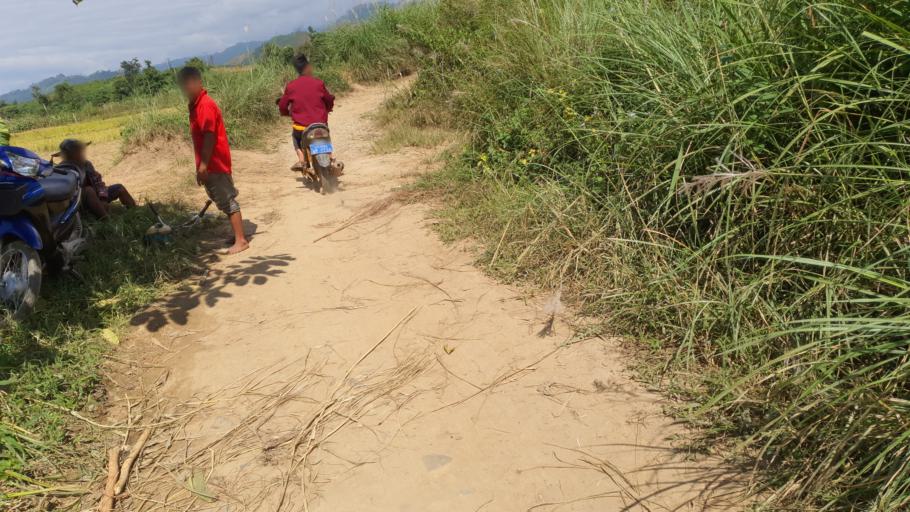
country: LA
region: Bolikhamxai
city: Bolikhan
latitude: 18.9087
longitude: 103.7423
